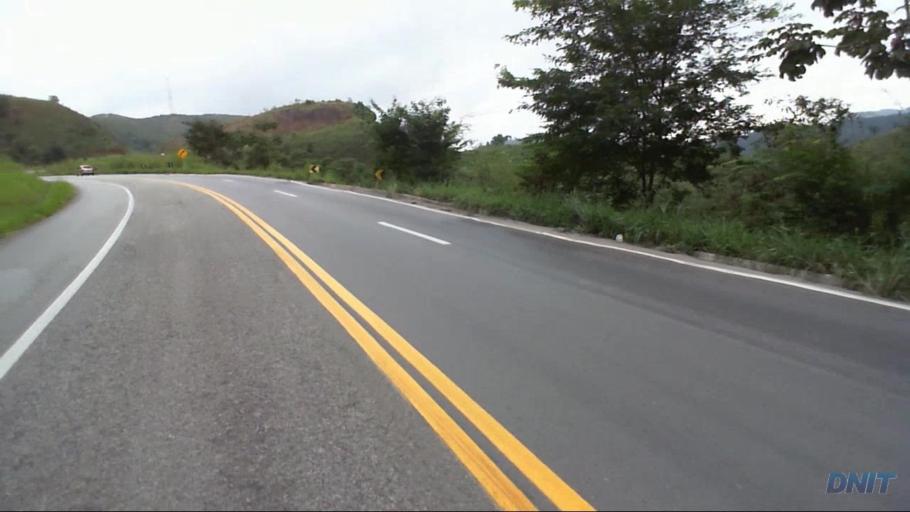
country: BR
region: Minas Gerais
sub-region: Nova Era
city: Nova Era
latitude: -19.6911
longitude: -42.9922
